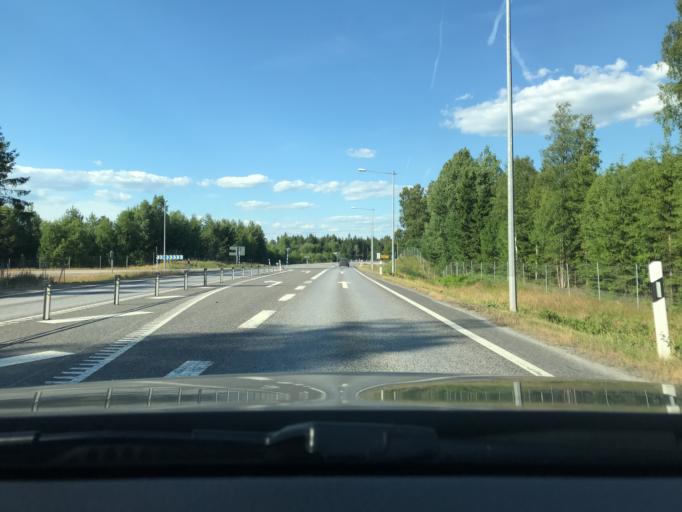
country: SE
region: Kronoberg
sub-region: Alvesta Kommun
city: Vislanda
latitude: 56.6847
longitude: 14.3193
